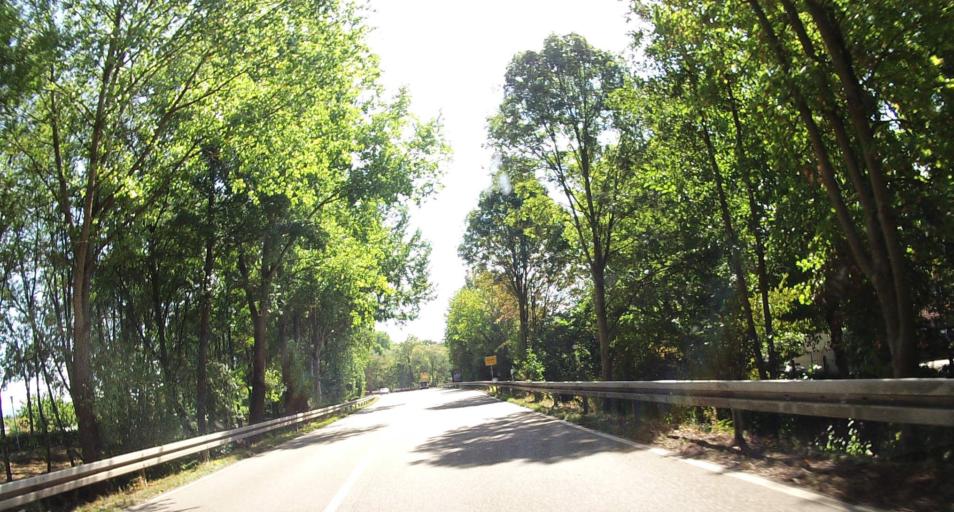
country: DE
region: Baden-Wuerttemberg
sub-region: Karlsruhe Region
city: Rastatt
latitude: 48.8456
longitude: 8.2188
